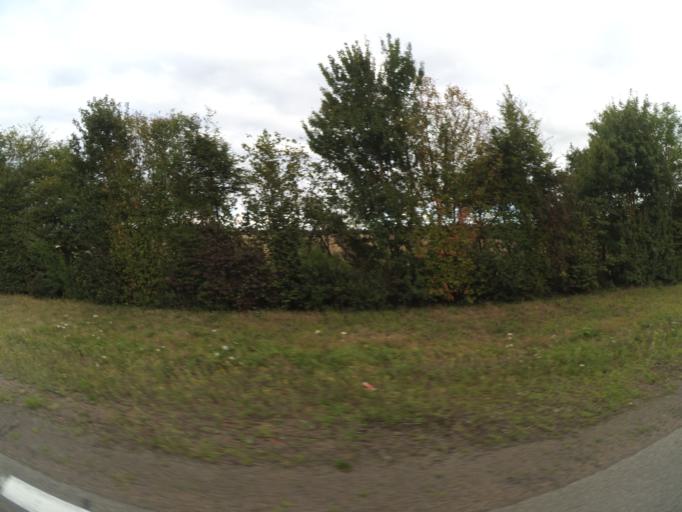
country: FR
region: Pays de la Loire
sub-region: Departement de la Vendee
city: Saligny
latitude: 46.8522
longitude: -1.4115
